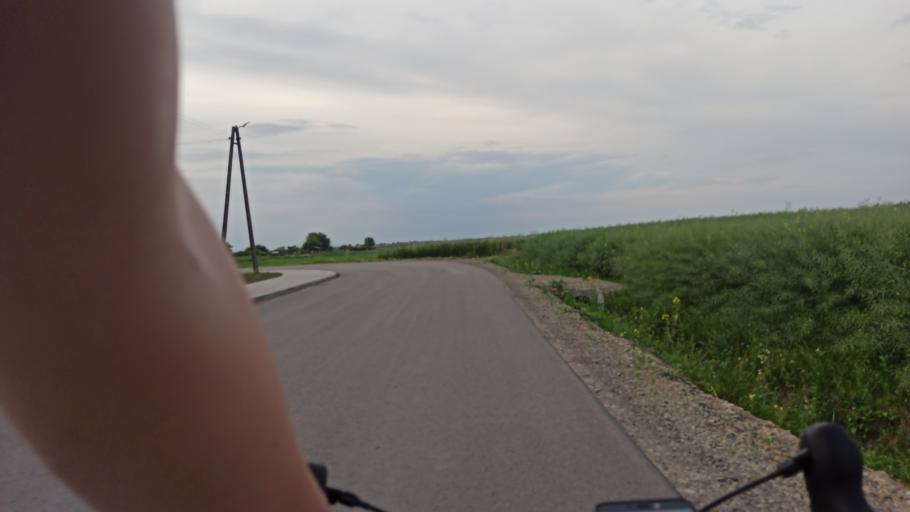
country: PL
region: Subcarpathian Voivodeship
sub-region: Powiat jaroslawski
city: Sosnica
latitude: 49.8974
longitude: 22.8380
